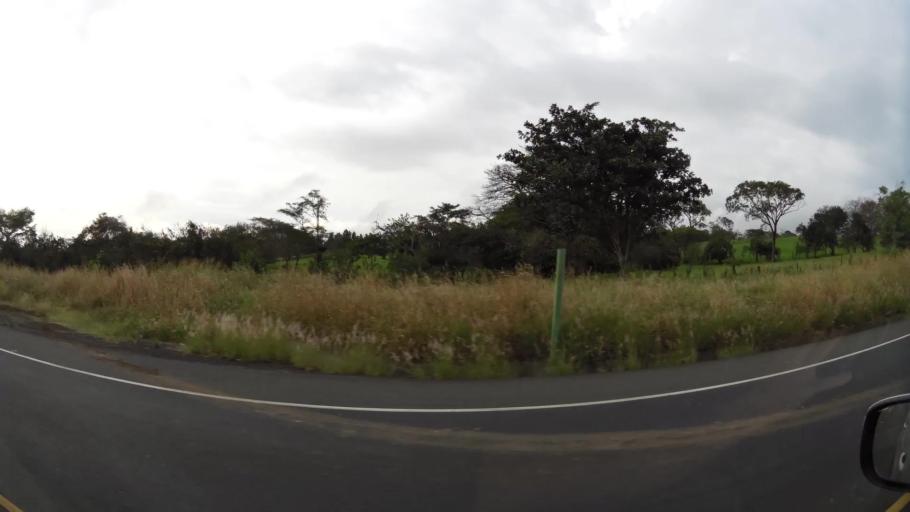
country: CR
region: Alajuela
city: Carrillos
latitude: 9.9645
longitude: -84.2939
